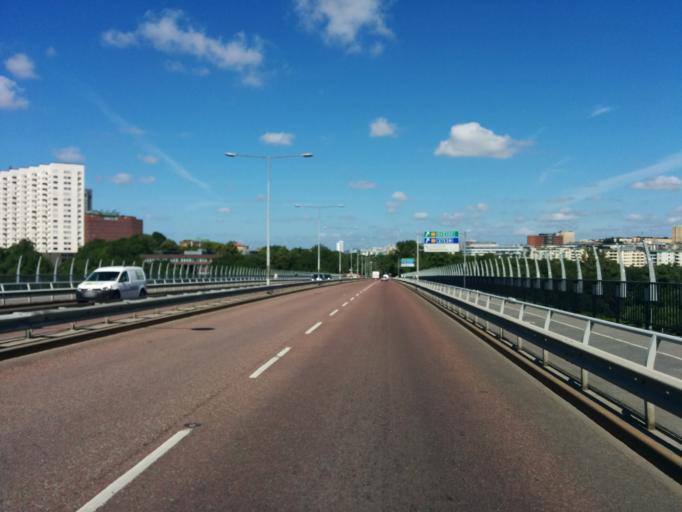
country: SE
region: Stockholm
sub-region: Stockholms Kommun
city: Arsta
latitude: 59.3249
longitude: 18.0271
